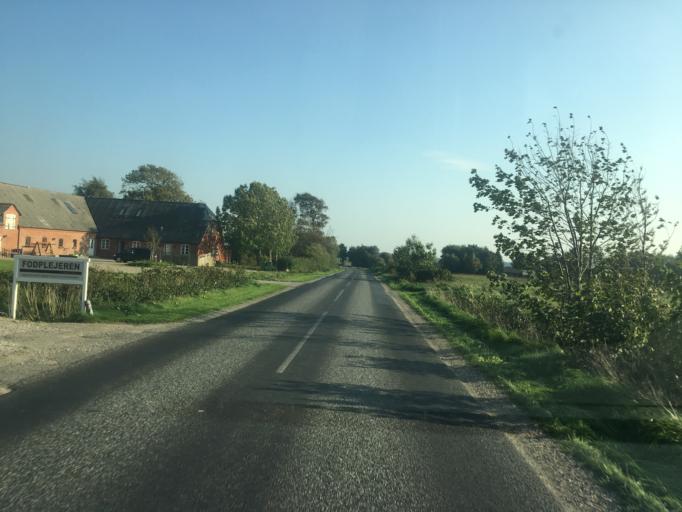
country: DE
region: Schleswig-Holstein
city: Bramstedtlund
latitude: 54.9476
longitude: 9.0603
